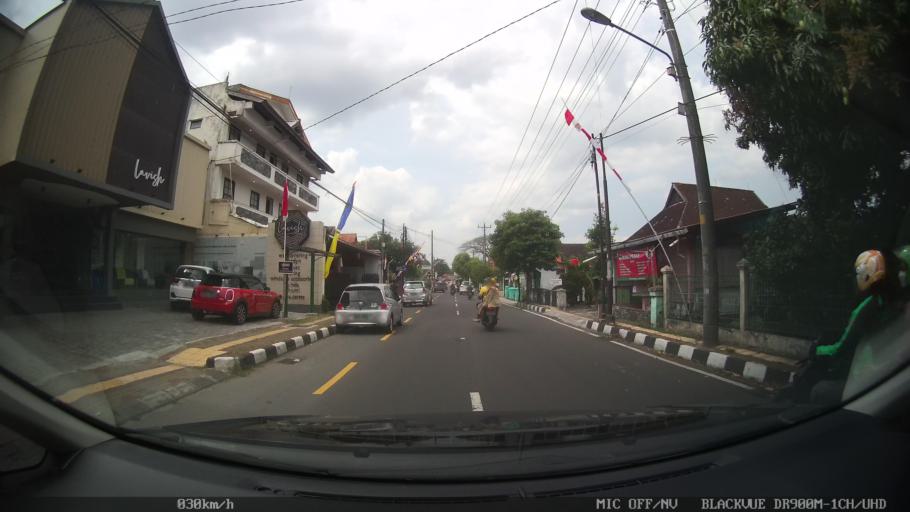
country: ID
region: Daerah Istimewa Yogyakarta
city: Yogyakarta
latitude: -7.7861
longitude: 110.3853
